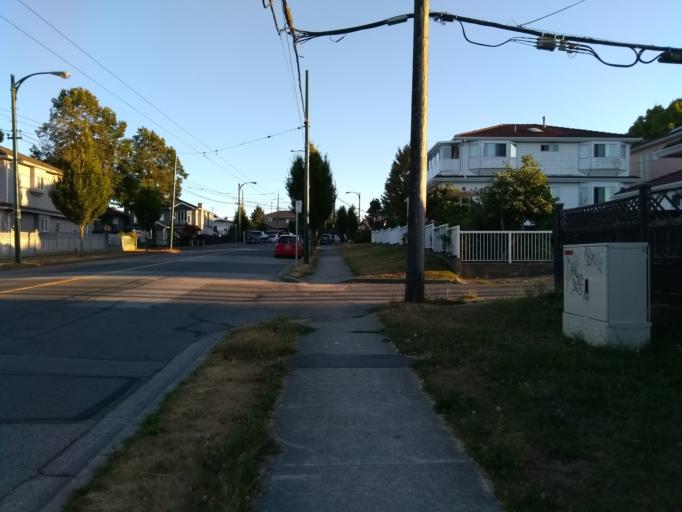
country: CA
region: British Columbia
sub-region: Fraser Valley Regional District
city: North Vancouver
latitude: 49.2459
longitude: -123.0418
